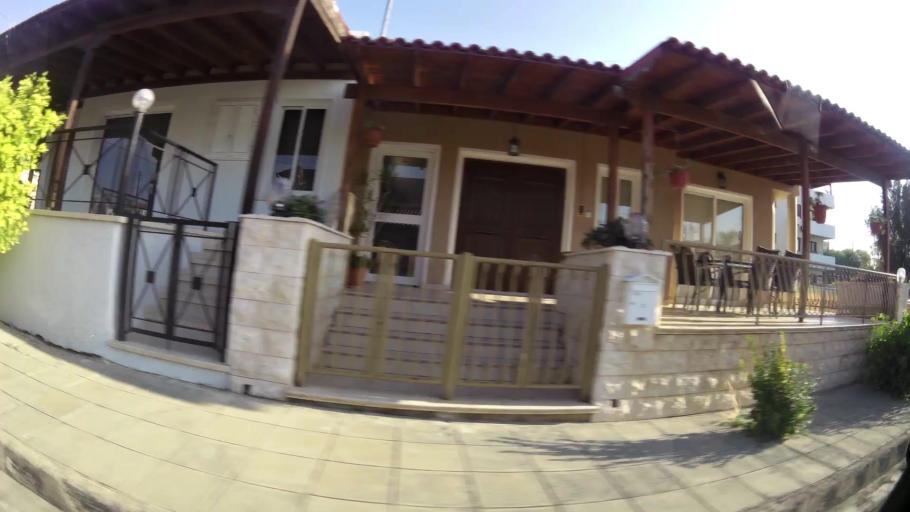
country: CY
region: Larnaka
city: Larnaca
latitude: 34.9289
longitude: 33.6001
